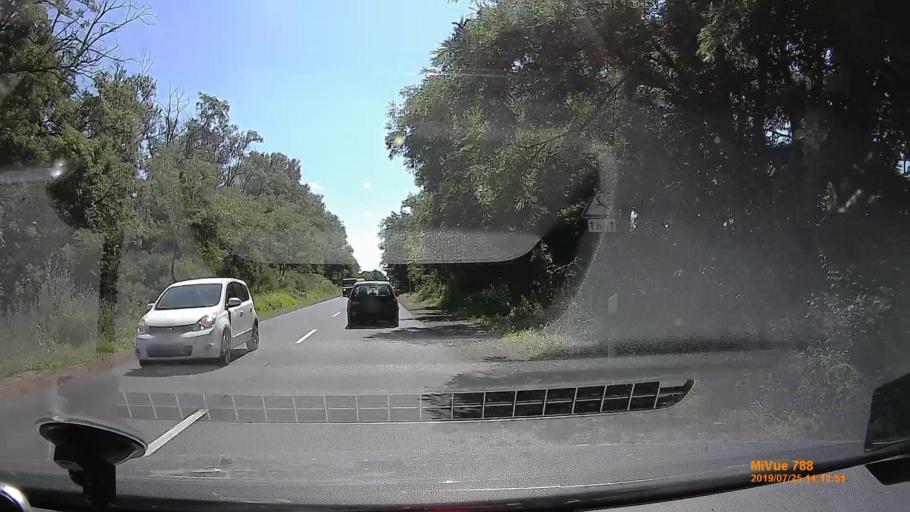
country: HU
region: Szabolcs-Szatmar-Bereg
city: Nagykallo
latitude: 47.8972
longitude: 21.7970
